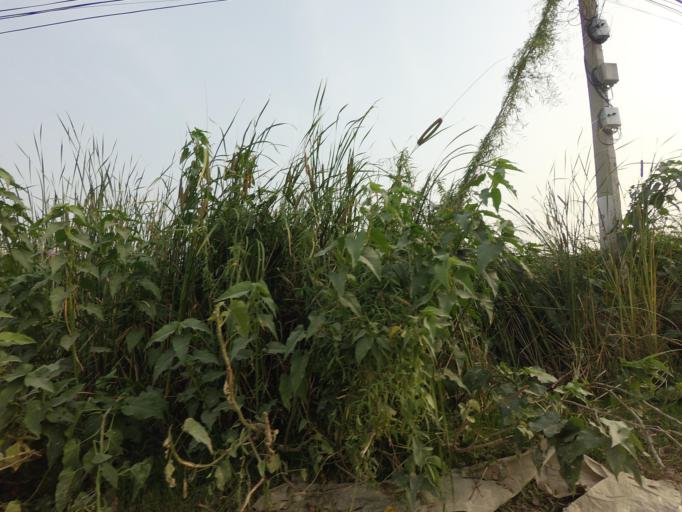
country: NP
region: Western Region
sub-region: Lumbini Zone
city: Bhairahawa
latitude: 27.5079
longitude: 83.4590
